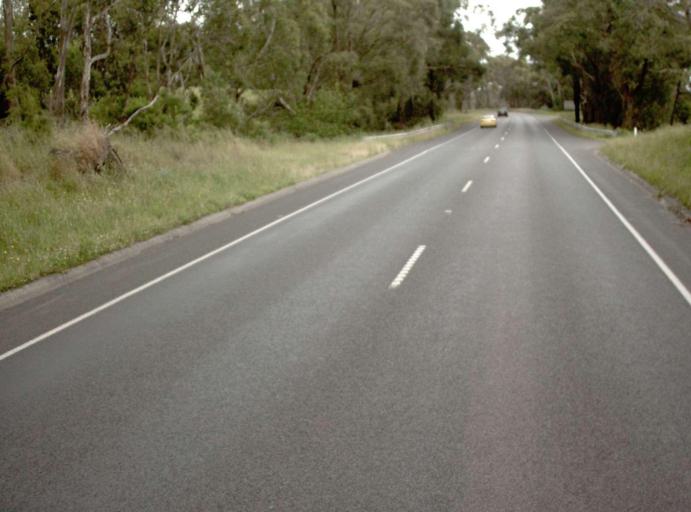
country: AU
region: Victoria
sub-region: Cardinia
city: Koo-Wee-Rup
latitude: -38.3380
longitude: 145.6264
